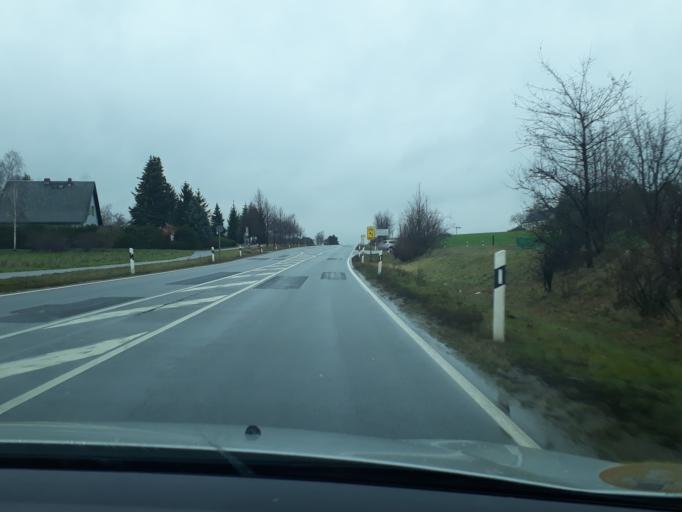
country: DE
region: Saxony
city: Bautzen
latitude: 51.1998
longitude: 14.4665
